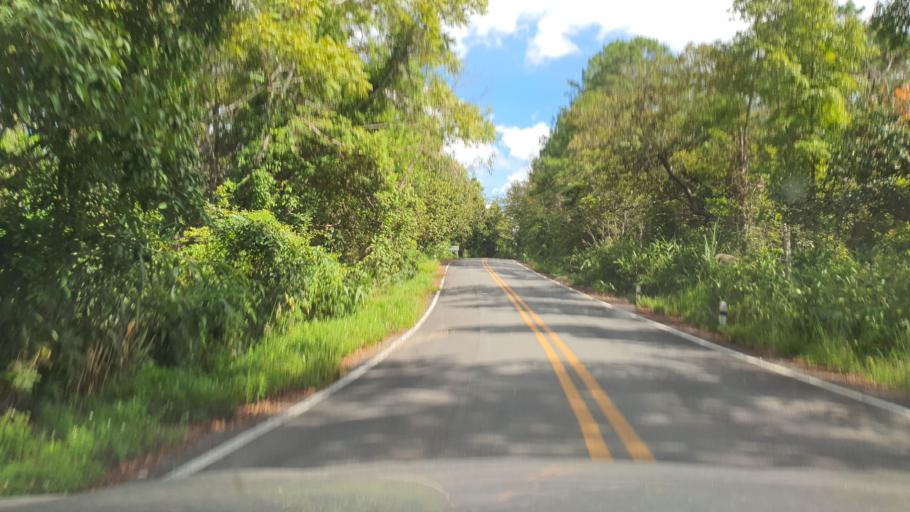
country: TH
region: Chiang Rai
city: Wiang Pa Pao
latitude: 19.3145
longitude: 99.3835
